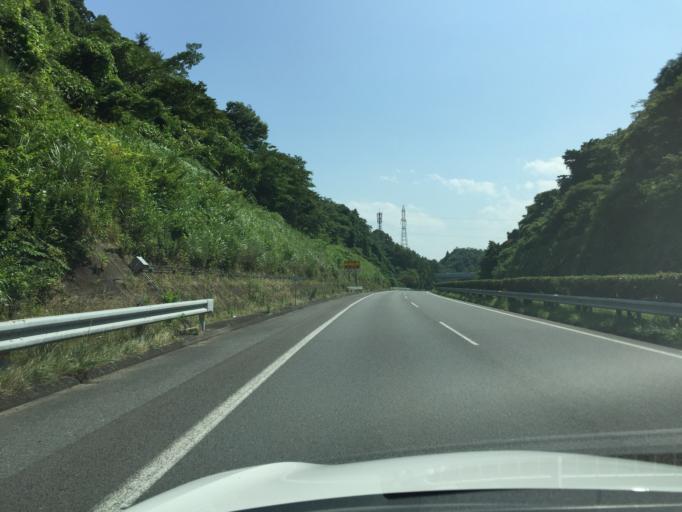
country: JP
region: Fukushima
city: Iwaki
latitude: 36.9905
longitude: 140.8050
